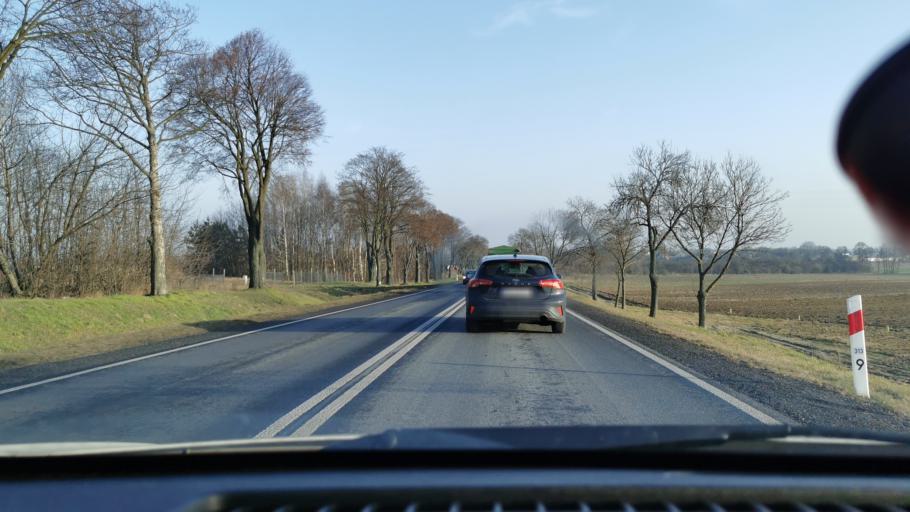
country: PL
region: Lodz Voivodeship
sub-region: Powiat sieradzki
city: Wroblew
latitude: 51.6158
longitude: 18.6019
